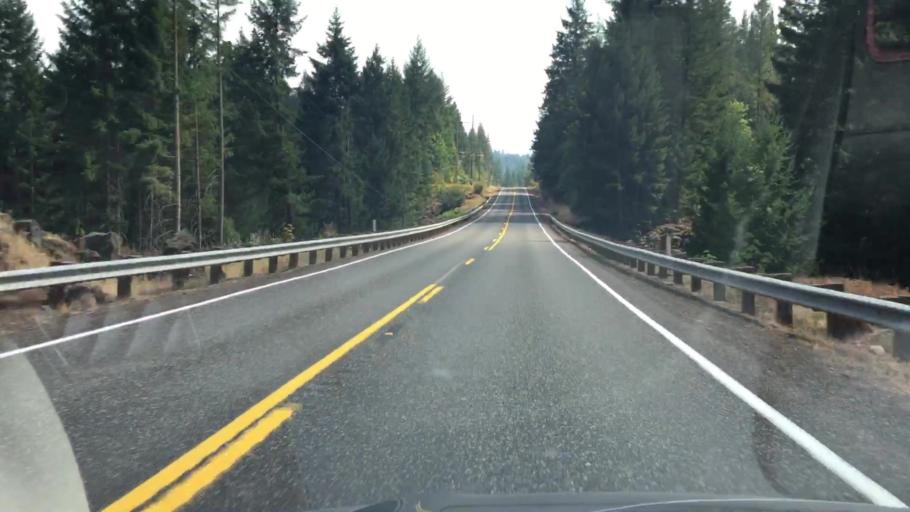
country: US
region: Washington
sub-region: Klickitat County
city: White Salmon
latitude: 45.8721
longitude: -121.5158
